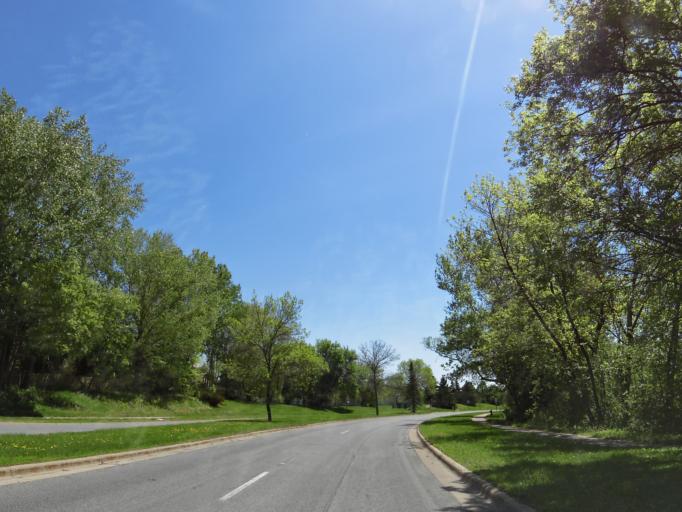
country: US
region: Minnesota
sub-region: Hennepin County
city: Edina
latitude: 44.8345
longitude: -93.3940
